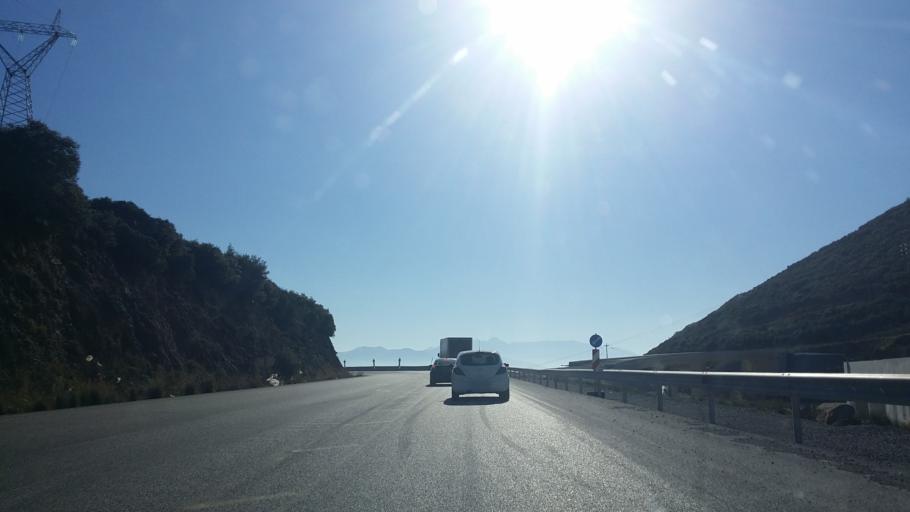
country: GR
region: West Greece
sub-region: Nomos Aitolias kai Akarnanias
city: Galatas
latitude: 38.3589
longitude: 21.6594
